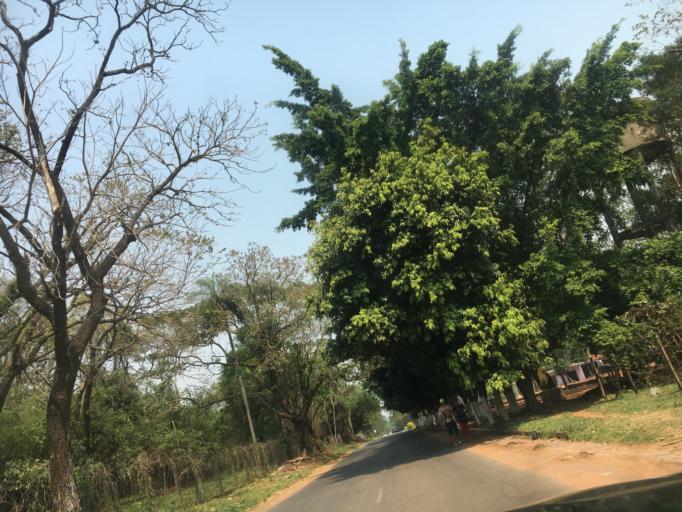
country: PY
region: Central
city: Villa Elisa
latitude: -25.3749
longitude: -57.5905
